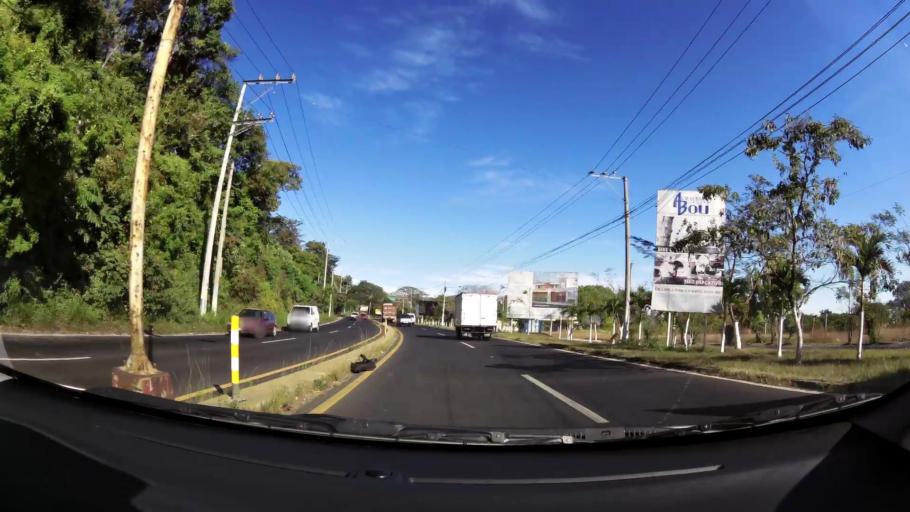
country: SV
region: Santa Ana
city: Santa Ana
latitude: 13.9574
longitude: -89.5681
